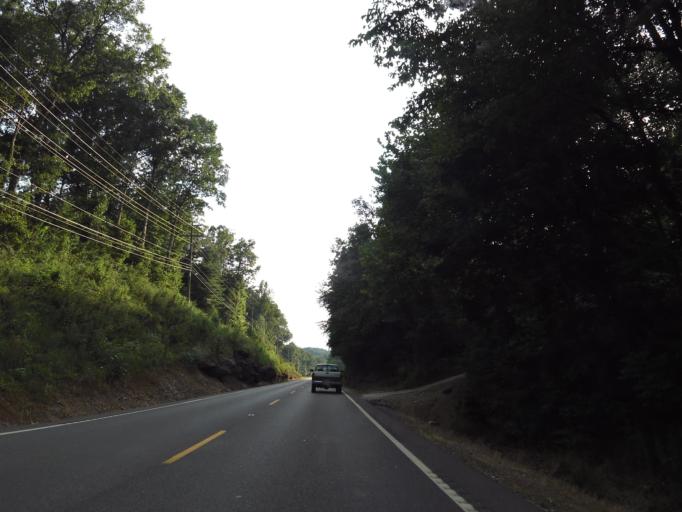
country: US
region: Tennessee
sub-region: Roane County
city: Oliver Springs
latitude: 36.0410
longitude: -84.3759
